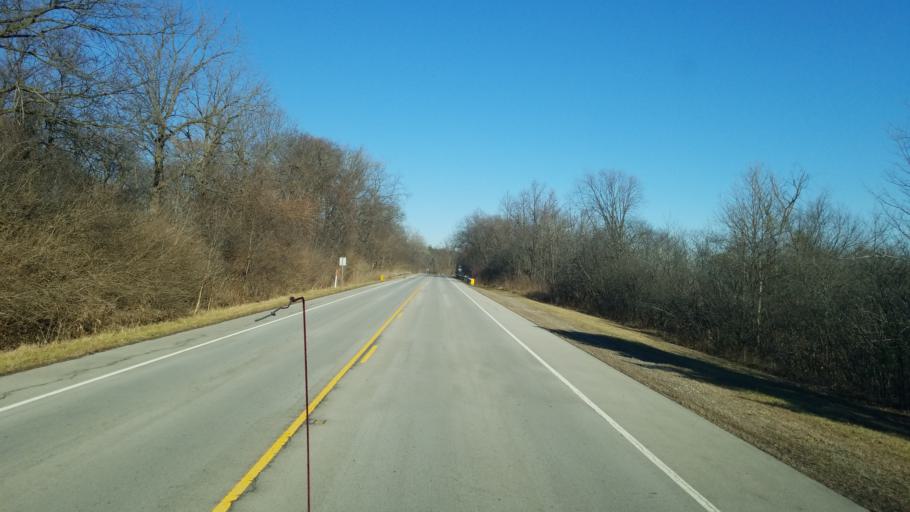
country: US
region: Ohio
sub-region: Lucas County
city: Waterville
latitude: 41.4771
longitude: -83.7498
